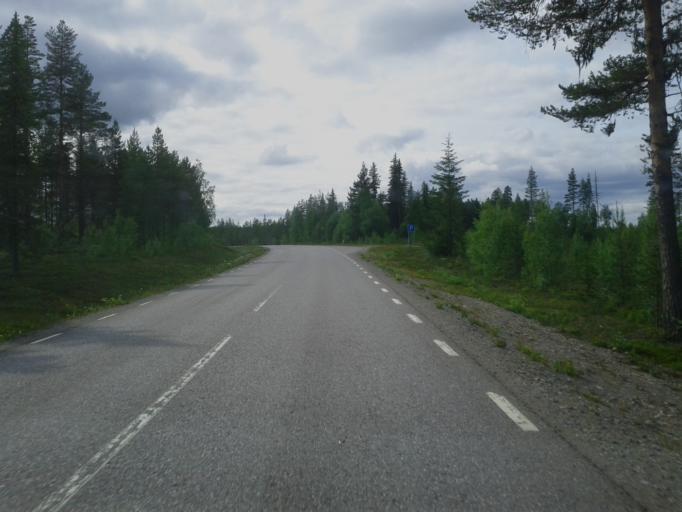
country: SE
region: Vaesterbotten
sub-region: Sorsele Kommun
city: Sorsele
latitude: 65.2863
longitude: 17.8441
